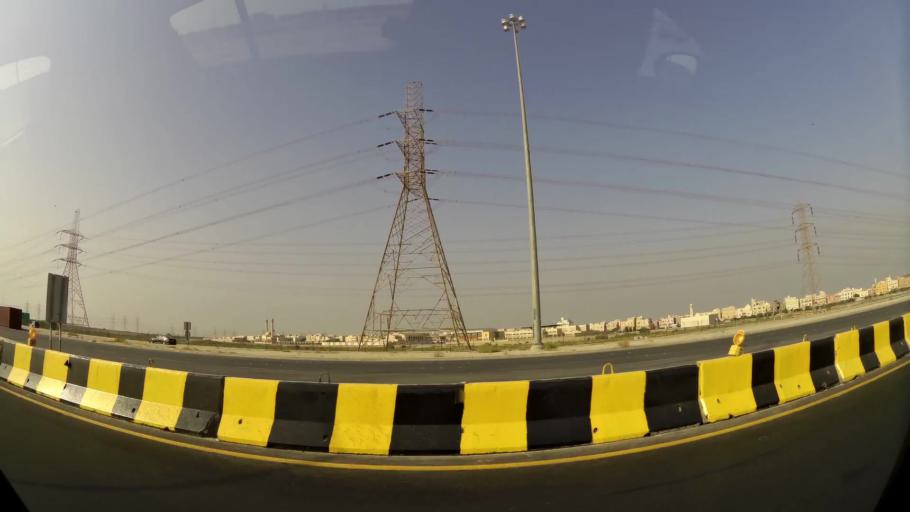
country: KW
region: Al Asimah
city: Ar Rabiyah
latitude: 29.2955
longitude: 47.7926
